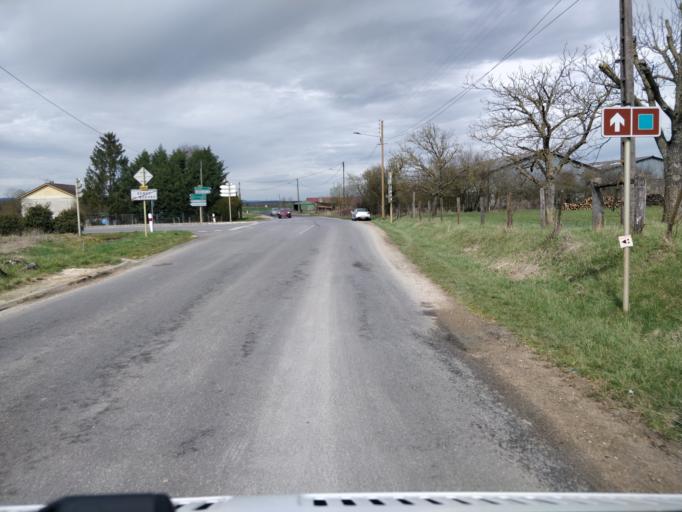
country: FR
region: Lorraine
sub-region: Departement de la Meuse
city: Vigneulles-les-Hattonchatel
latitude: 48.9637
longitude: 5.8228
